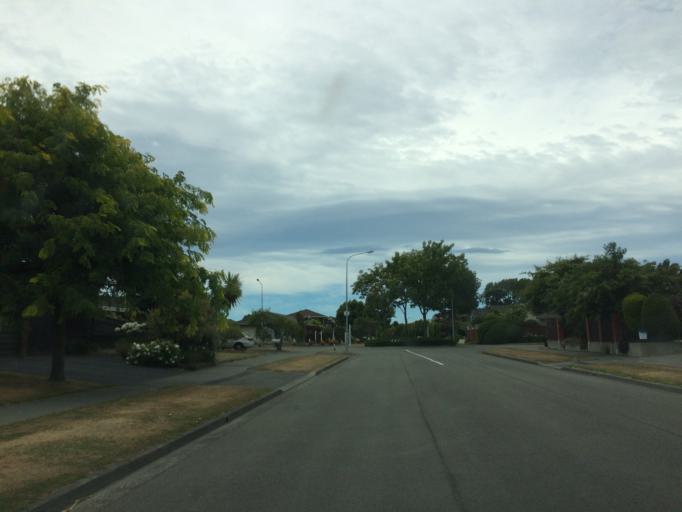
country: NZ
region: Canterbury
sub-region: Christchurch City
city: Christchurch
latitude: -43.5256
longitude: 172.5625
